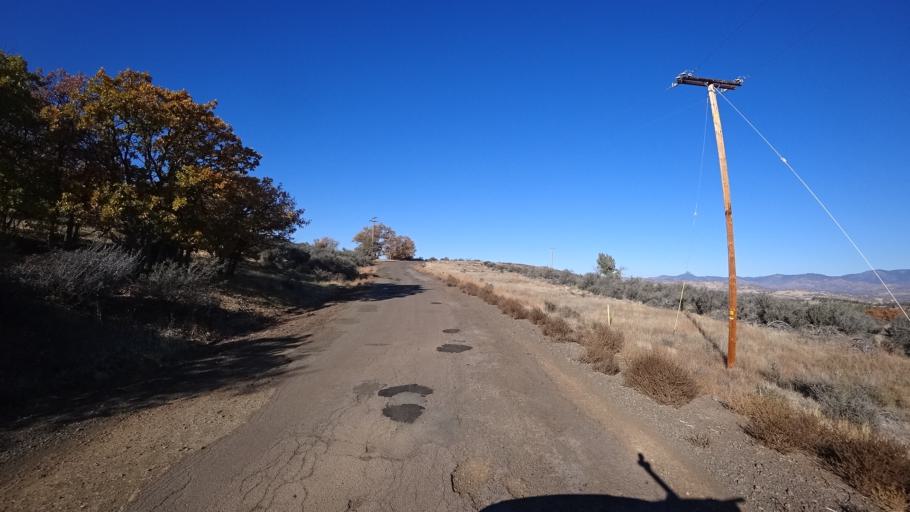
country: US
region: California
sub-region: Siskiyou County
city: Montague
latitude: 41.9036
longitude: -122.4326
